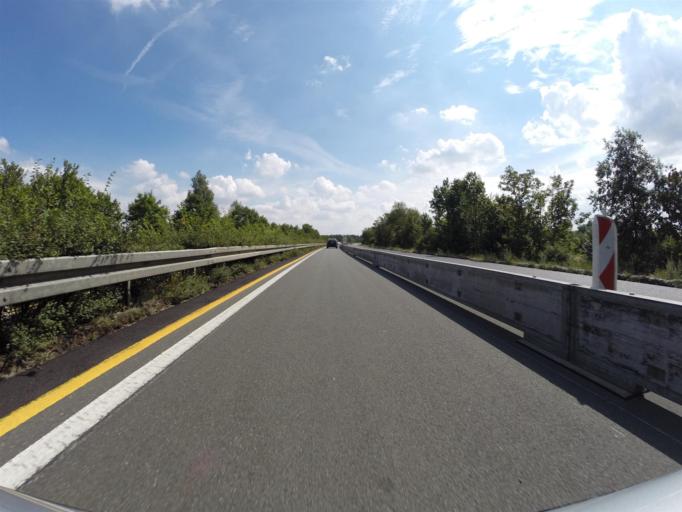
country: DE
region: North Rhine-Westphalia
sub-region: Regierungsbezirk Detmold
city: Hovelhof
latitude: 51.8165
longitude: 8.7008
